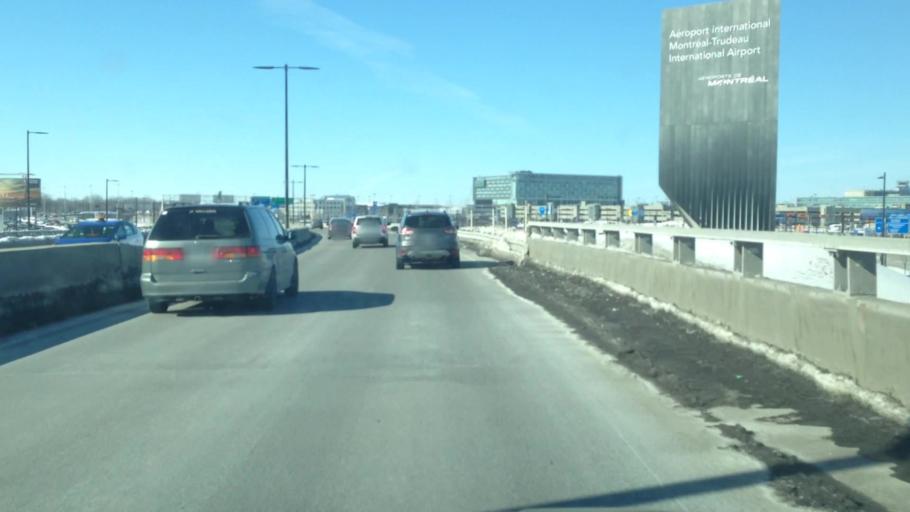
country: CA
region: Quebec
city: Dorval
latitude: 45.4524
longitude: -73.7422
